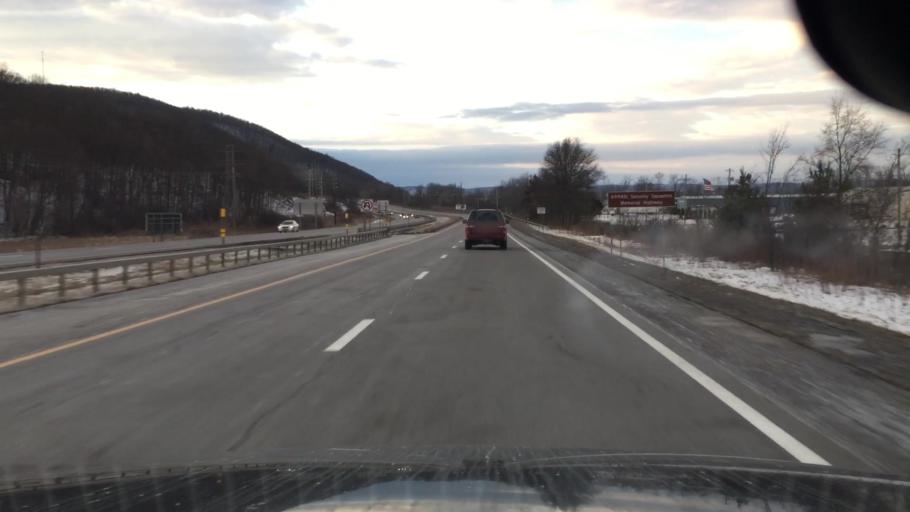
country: US
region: New York
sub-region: Chemung County
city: Elmira Heights
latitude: 42.1434
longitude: -76.8056
